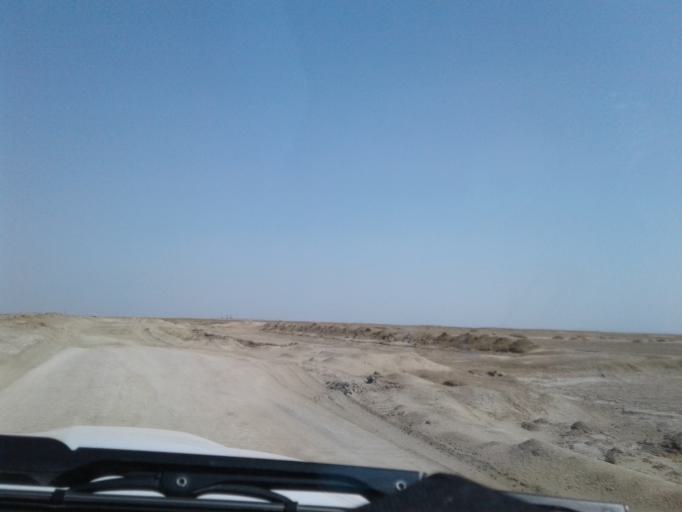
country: IR
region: Golestan
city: Gomishan
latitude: 37.8316
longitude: 53.9215
